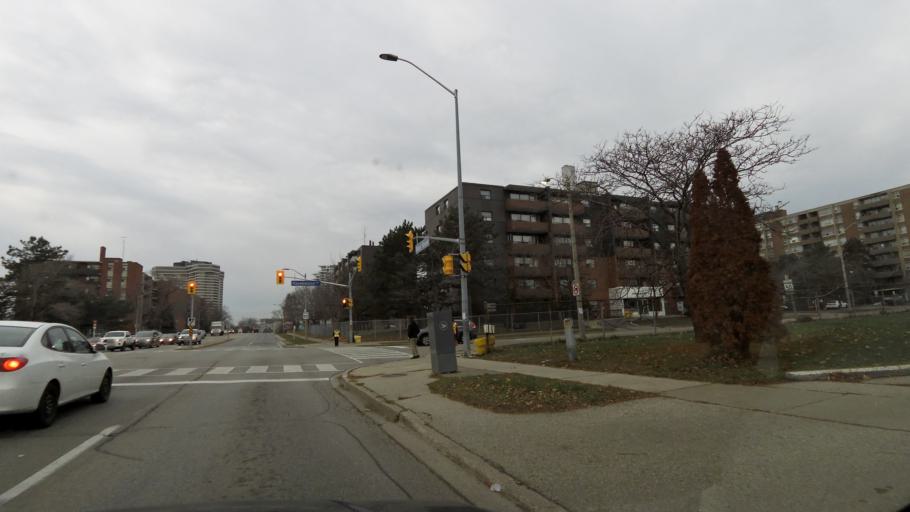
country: CA
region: Ontario
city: Etobicoke
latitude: 43.6194
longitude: -79.5918
